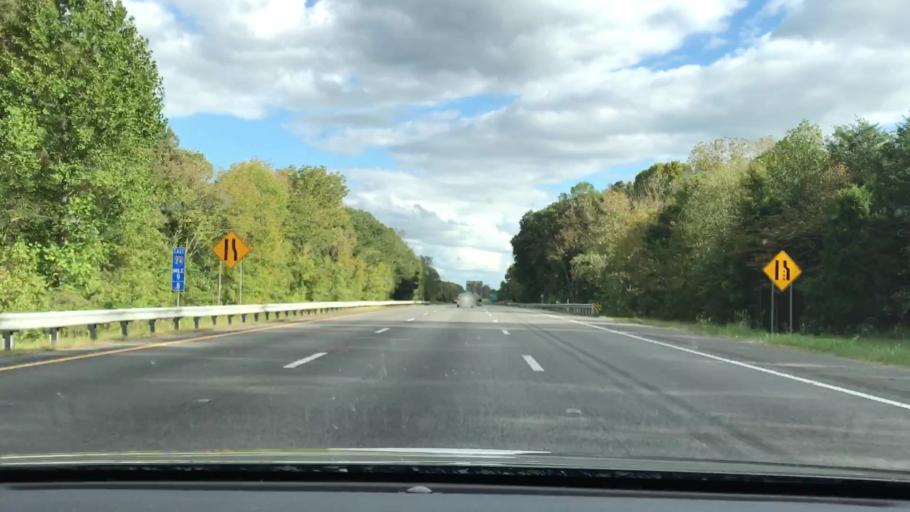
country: US
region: Tennessee
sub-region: Montgomery County
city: Clarksville
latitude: 36.5336
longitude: -87.2329
